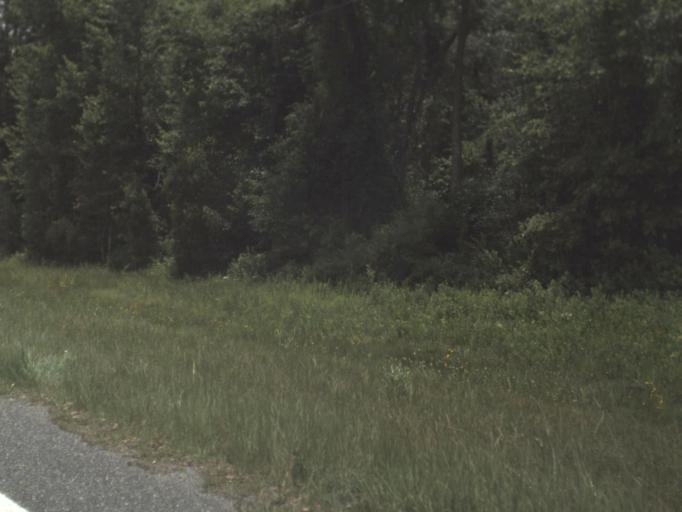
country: US
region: Florida
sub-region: Union County
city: Lake Butler
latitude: 29.9819
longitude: -82.2414
